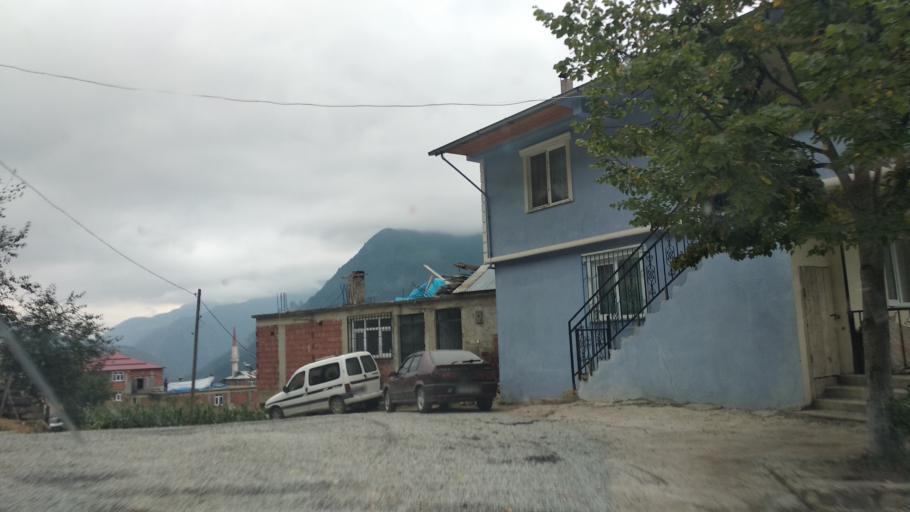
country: TR
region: Giresun
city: Dogankent
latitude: 40.7479
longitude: 38.9852
